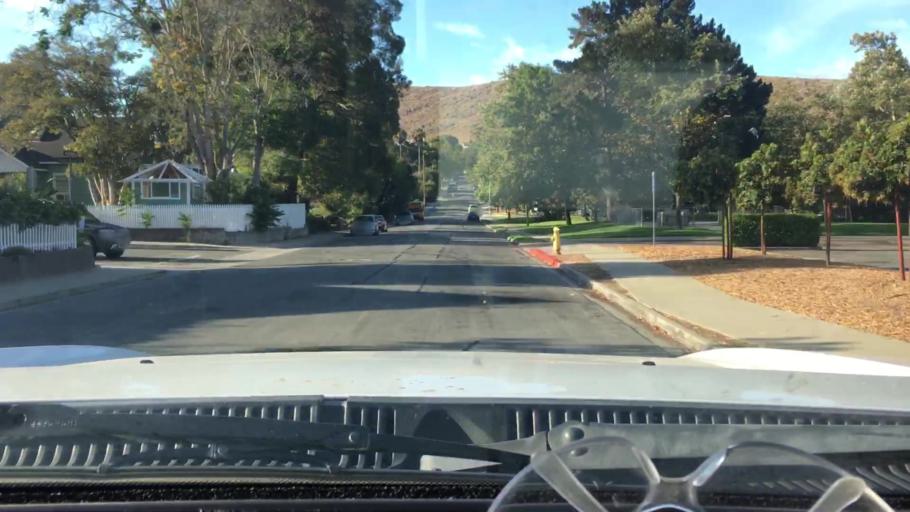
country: US
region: California
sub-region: San Luis Obispo County
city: San Luis Obispo
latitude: 35.2687
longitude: -120.6582
